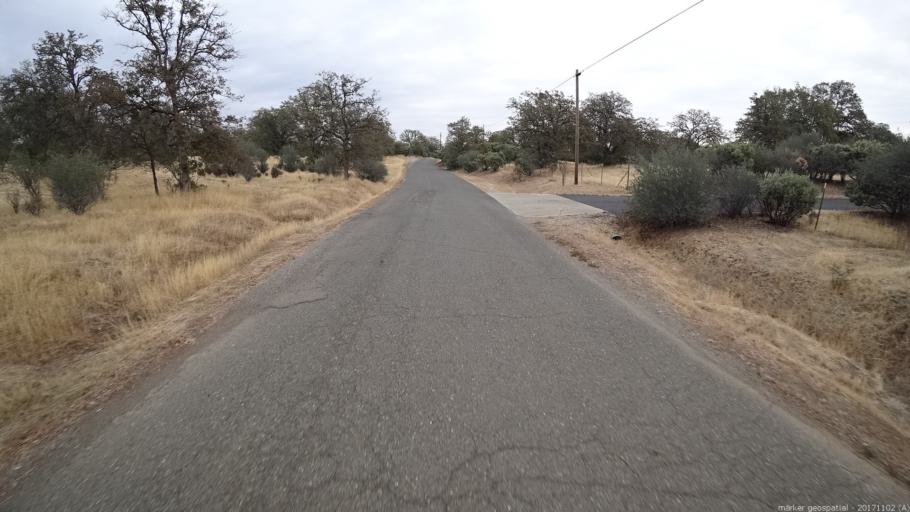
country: US
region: California
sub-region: Shasta County
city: Shasta
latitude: 40.6312
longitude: -122.4372
